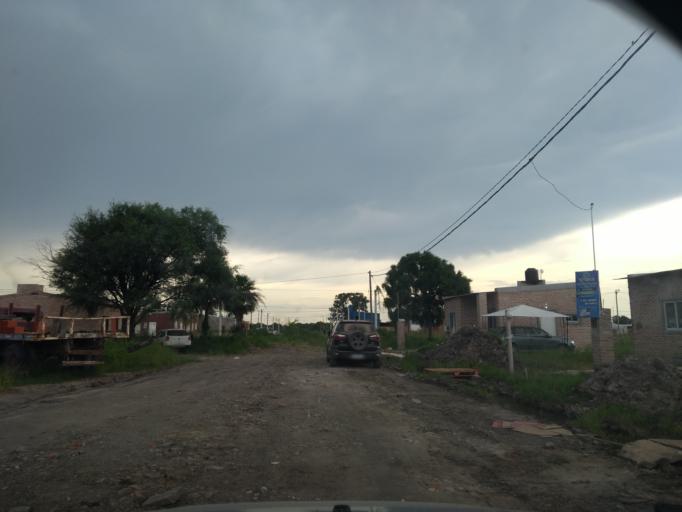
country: AR
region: Chaco
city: Resistencia
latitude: -27.4675
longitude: -59.0315
